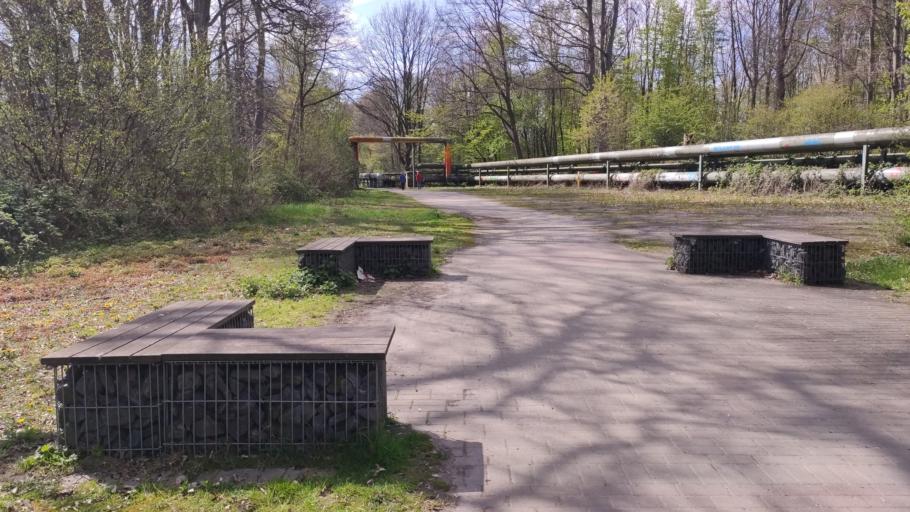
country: DE
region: North Rhine-Westphalia
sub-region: Regierungsbezirk Arnsberg
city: Herne
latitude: 51.5071
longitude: 7.2499
